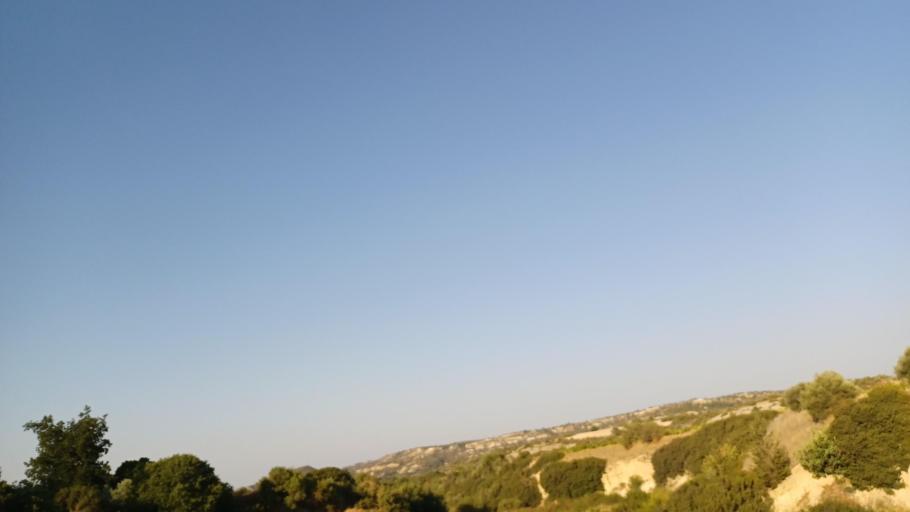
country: CY
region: Limassol
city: Pissouri
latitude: 34.7106
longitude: 32.6810
